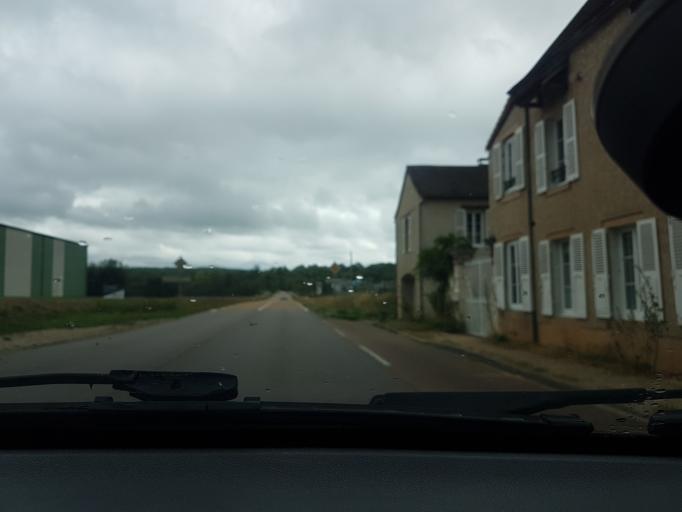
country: FR
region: Bourgogne
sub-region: Departement de l'Yonne
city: Vermenton
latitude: 47.6018
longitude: 3.7632
